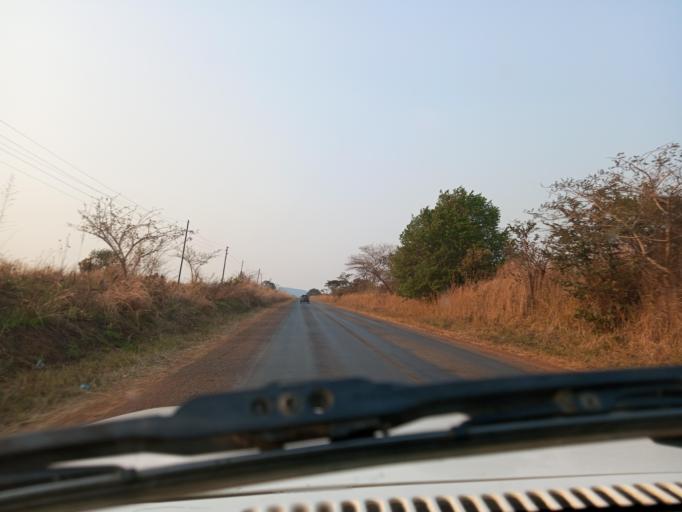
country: ZM
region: Northern
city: Mpika
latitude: -11.9033
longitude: 31.4137
